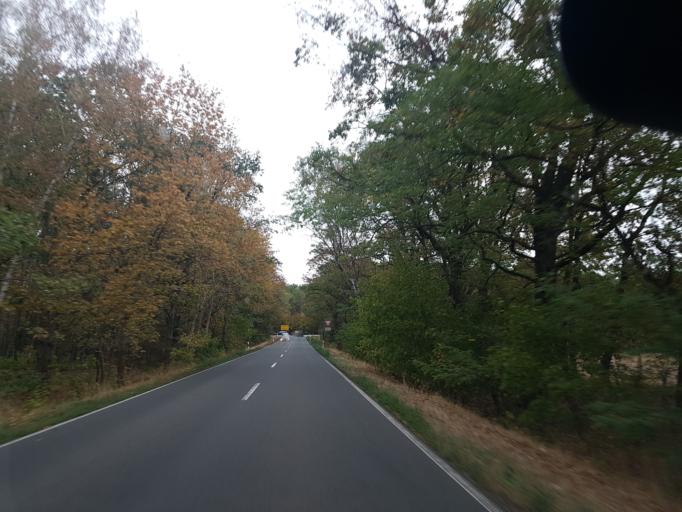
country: DE
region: Saxony-Anhalt
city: Elster
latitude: 51.8122
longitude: 12.8743
